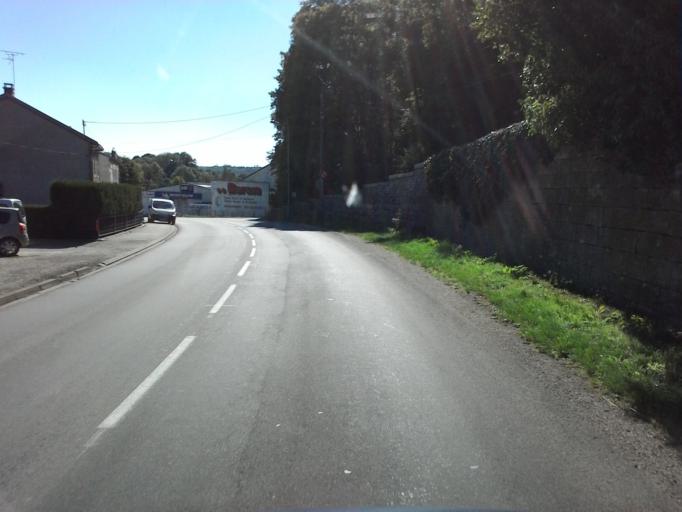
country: FR
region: Champagne-Ardenne
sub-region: Departement de la Haute-Marne
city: Chaumont
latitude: 48.1171
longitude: 5.1504
